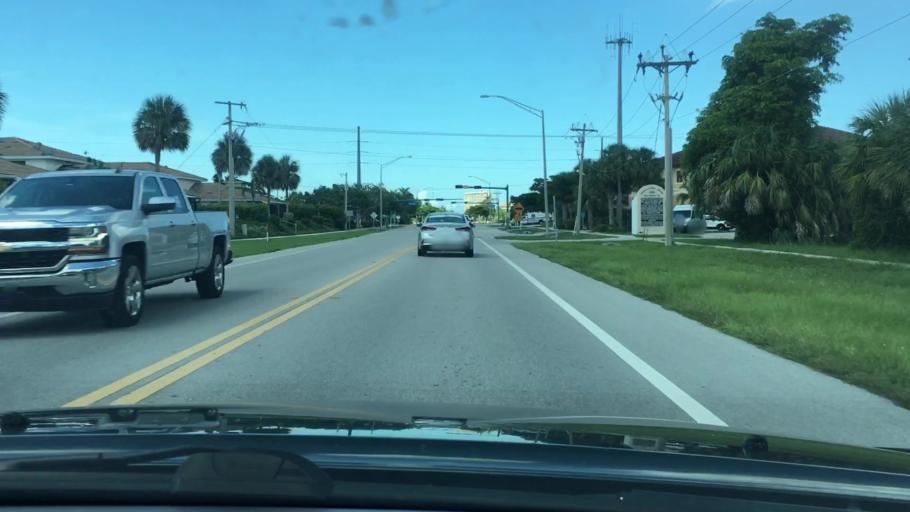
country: US
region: Florida
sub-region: Collier County
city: Marco
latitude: 25.9371
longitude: -81.7134
